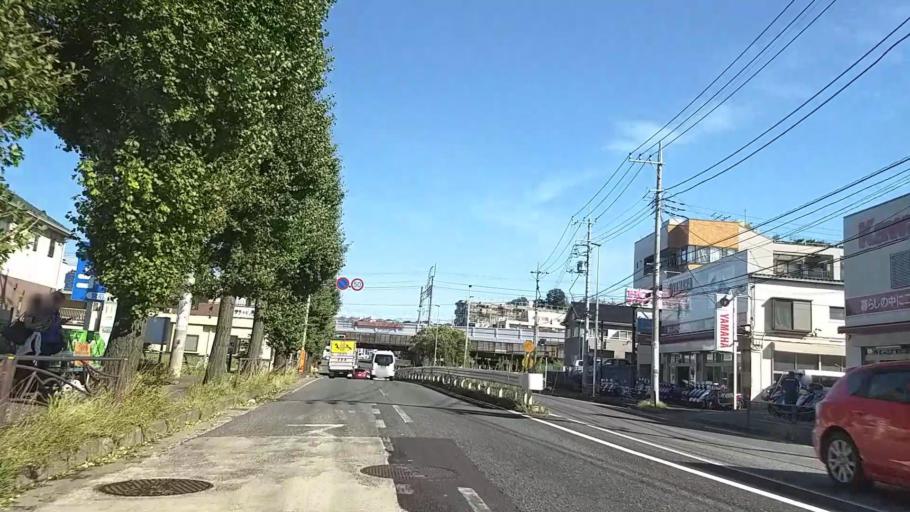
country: JP
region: Tokyo
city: Chofugaoka
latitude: 35.5778
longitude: 139.6114
